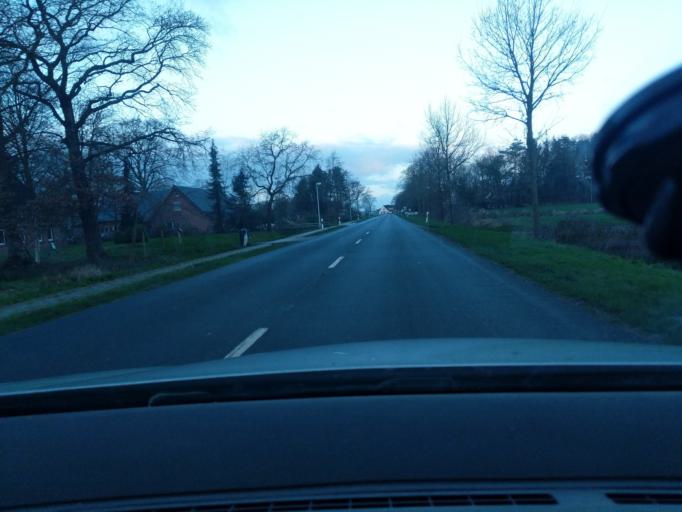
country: DE
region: Lower Saxony
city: Stinstedt
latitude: 53.6347
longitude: 8.9666
